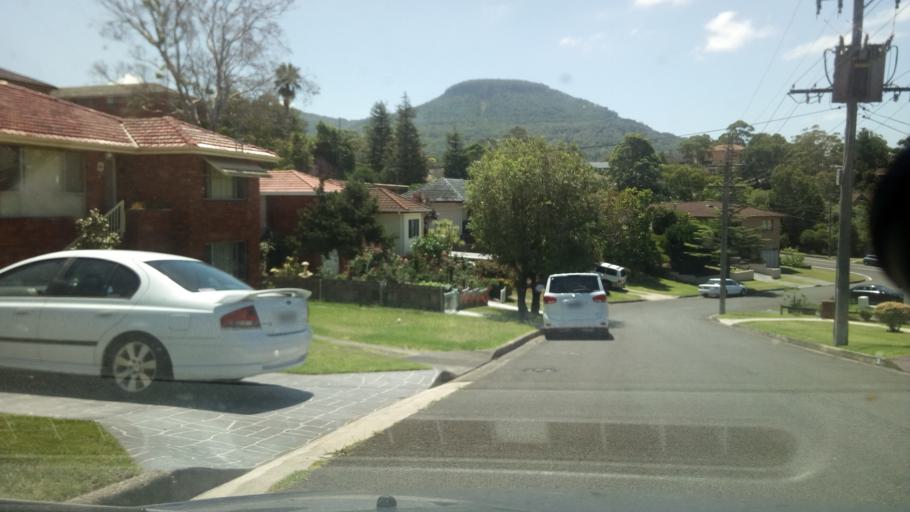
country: AU
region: New South Wales
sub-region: Wollongong
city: West Wollongong
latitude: -34.4277
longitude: 150.8563
